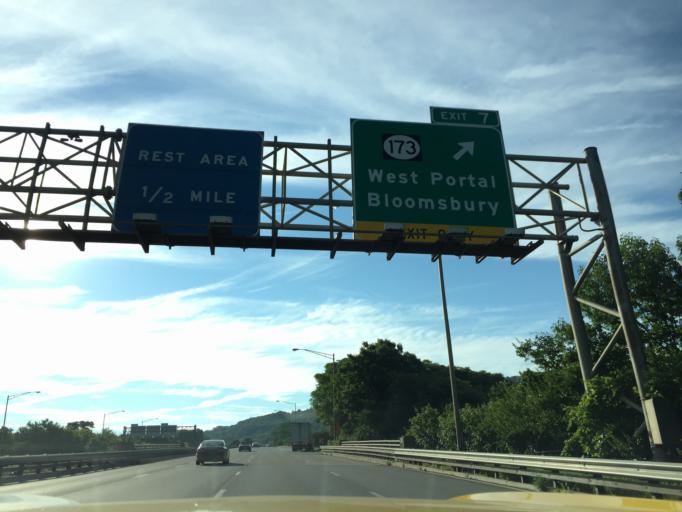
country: US
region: New Jersey
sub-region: Warren County
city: Alpha
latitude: 40.6601
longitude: -75.0717
